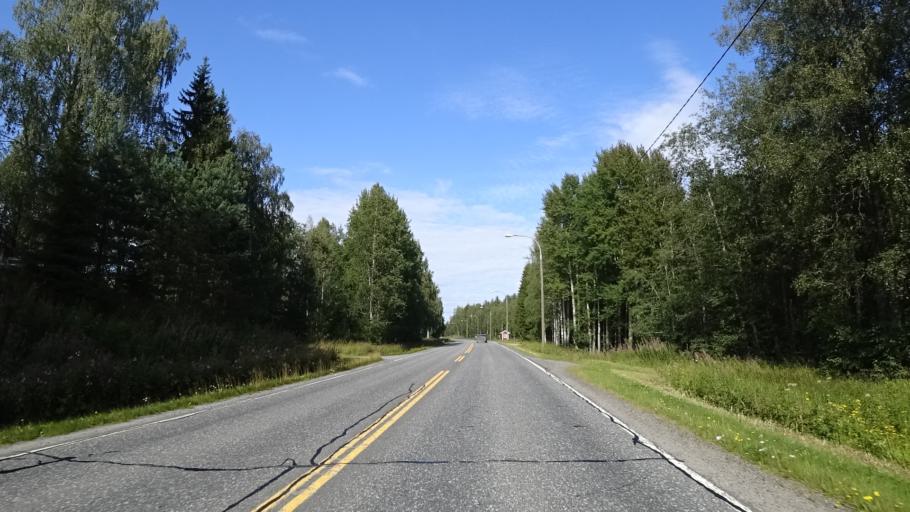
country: FI
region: North Karelia
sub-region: Joensuu
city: Eno
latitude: 62.7833
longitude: 30.0764
